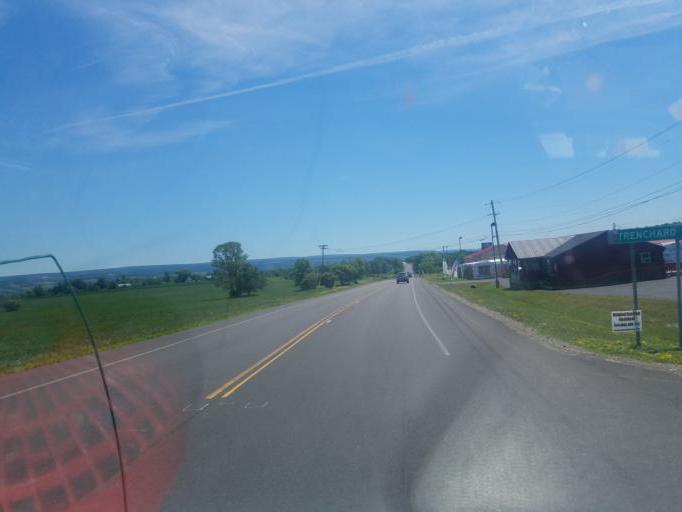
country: US
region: New York
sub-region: Yates County
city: Dundee
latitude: 42.5873
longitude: -76.9371
